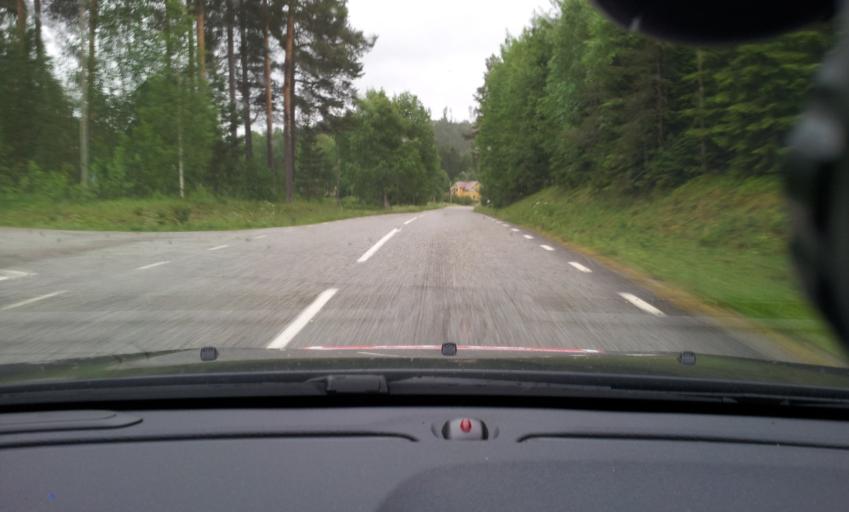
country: SE
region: Jaemtland
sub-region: Stroemsunds Kommun
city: Stroemsund
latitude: 63.3407
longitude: 15.7594
